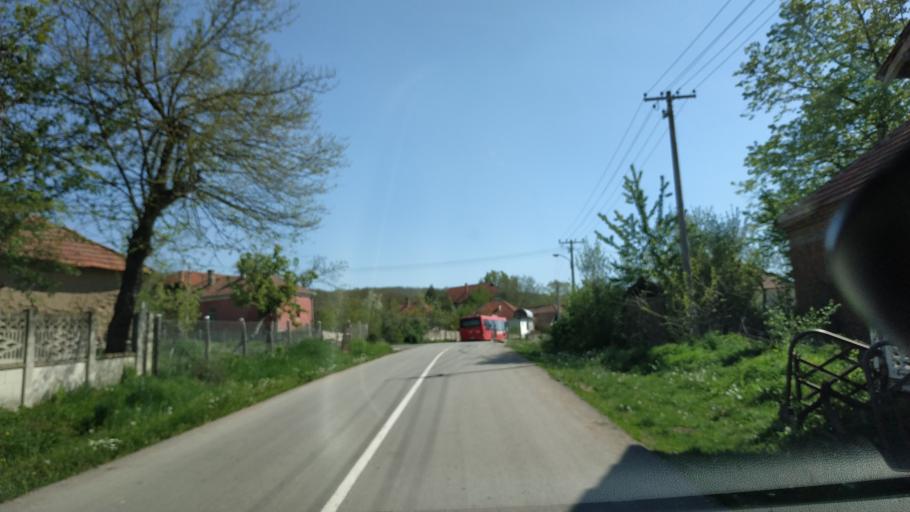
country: RS
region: Central Serbia
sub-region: Nisavski Okrug
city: Nis
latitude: 43.4646
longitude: 21.8618
